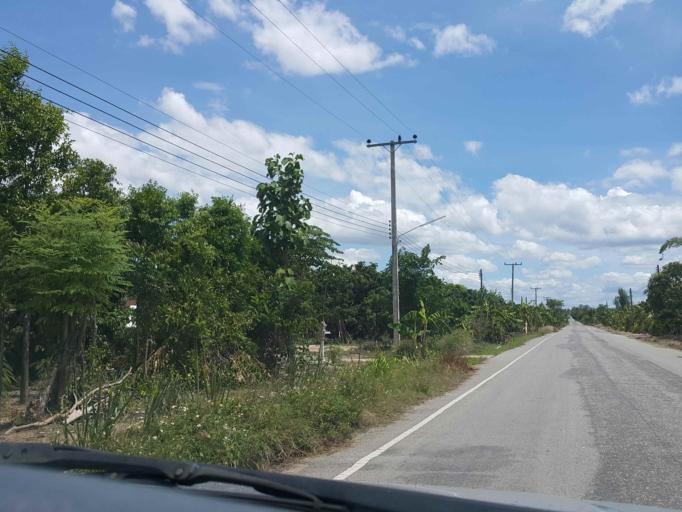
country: TH
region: Chiang Mai
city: Doi Lo
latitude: 18.5227
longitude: 98.7748
